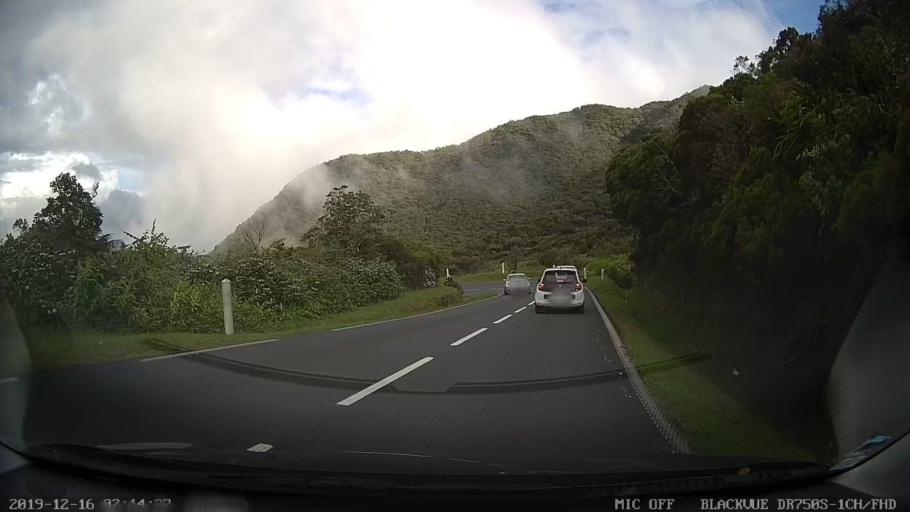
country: RE
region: Reunion
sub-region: Reunion
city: Cilaos
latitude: -21.1590
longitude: 55.5967
